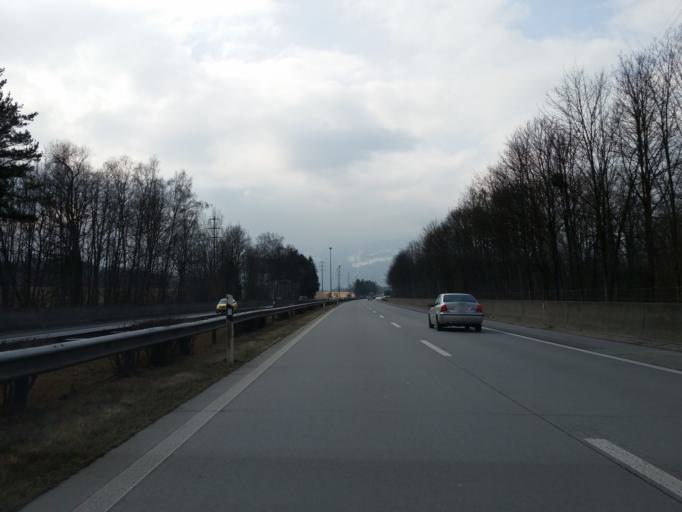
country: LI
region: Ruggell
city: Ruggell
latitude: 47.2384
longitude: 9.5139
